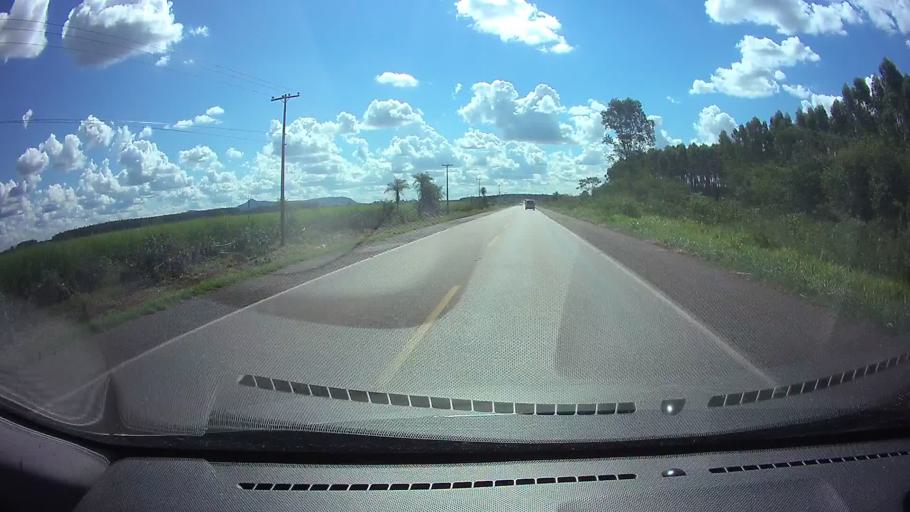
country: PY
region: Guaira
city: Coronel Martinez
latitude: -25.7638
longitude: -56.6843
